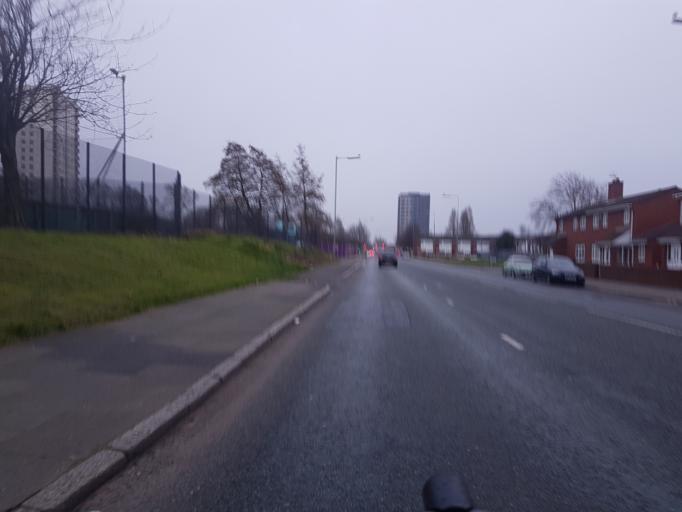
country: GB
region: England
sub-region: Liverpool
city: Liverpool
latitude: 53.4303
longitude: -2.9794
